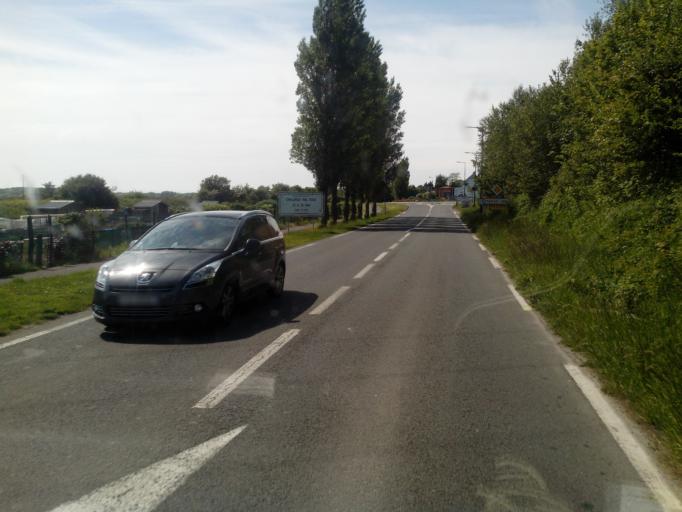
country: FR
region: Nord-Pas-de-Calais
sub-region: Departement du Pas-de-Calais
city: Etaples
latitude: 50.5091
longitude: 1.6574
